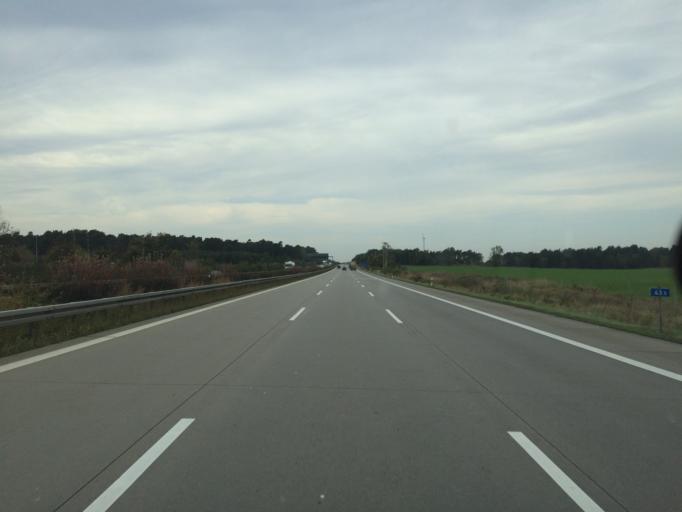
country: DE
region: Brandenburg
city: Ziesar
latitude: 52.2494
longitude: 12.2533
